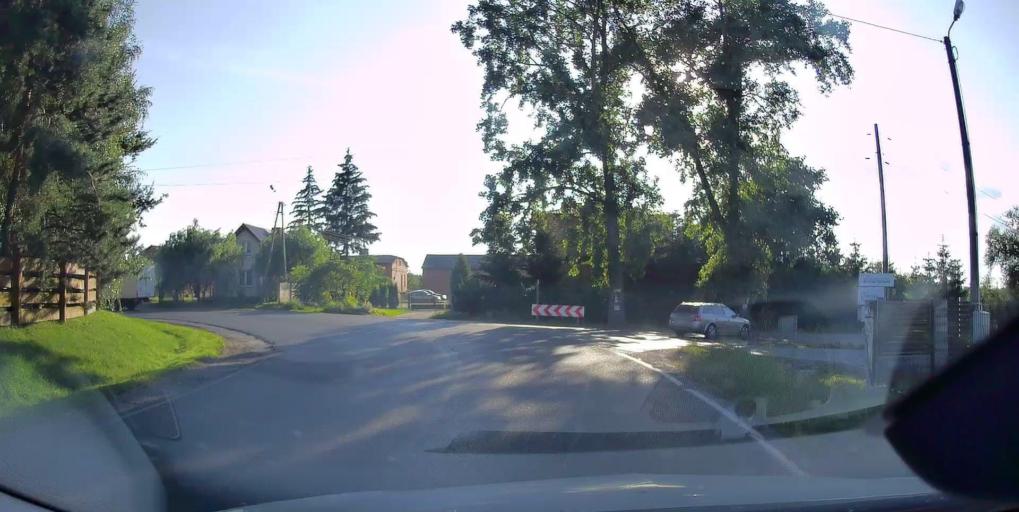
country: PL
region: Masovian Voivodeship
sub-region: Powiat grojecki
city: Bledow
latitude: 51.8095
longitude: 20.7001
